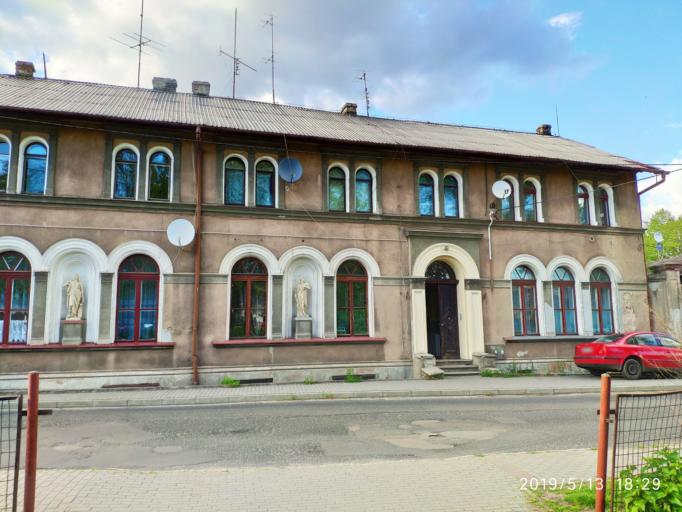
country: PL
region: Lubusz
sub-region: Powiat zielonogorski
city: Czerwiensk
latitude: 52.0130
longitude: 15.4254
